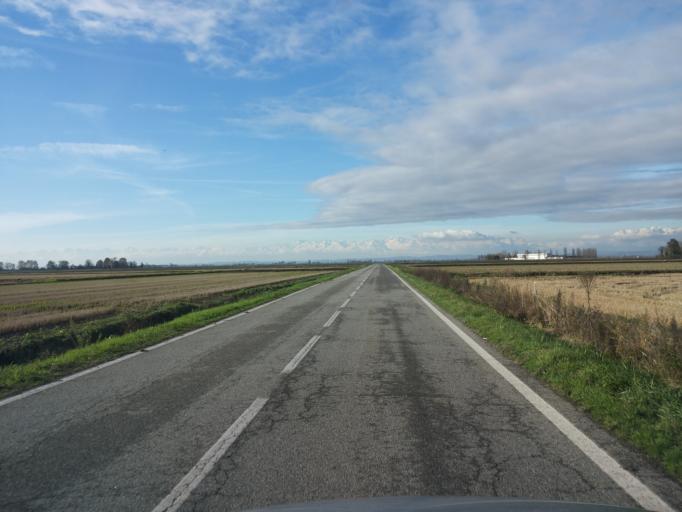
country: IT
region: Piedmont
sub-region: Provincia di Vercelli
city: Ronsecco
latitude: 45.2776
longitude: 8.2535
